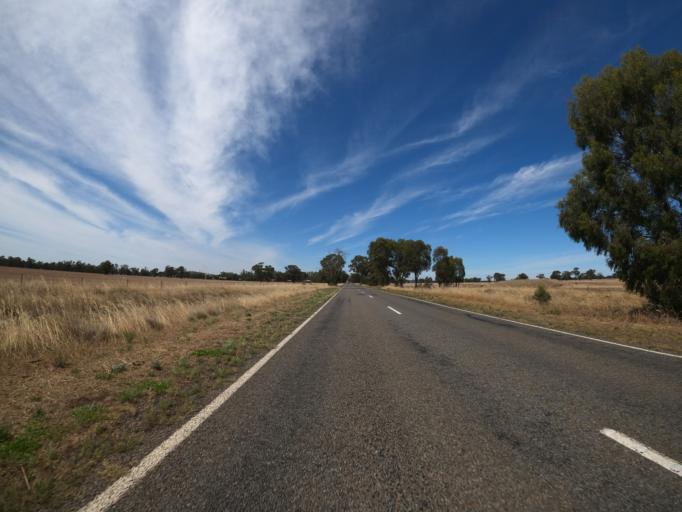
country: AU
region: Victoria
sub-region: Benalla
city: Benalla
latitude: -36.2868
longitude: 145.9523
